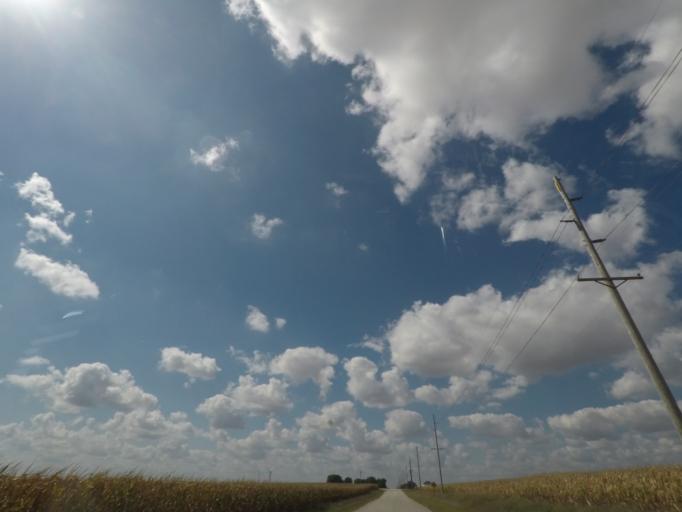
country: US
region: Iowa
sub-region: Story County
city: Nevada
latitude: 42.0345
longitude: -93.4030
